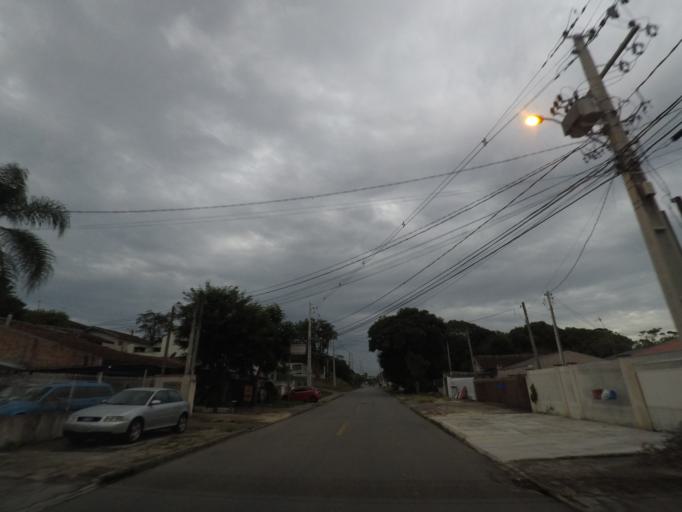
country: BR
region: Parana
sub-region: Curitiba
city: Curitiba
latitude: -25.4673
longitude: -49.3123
